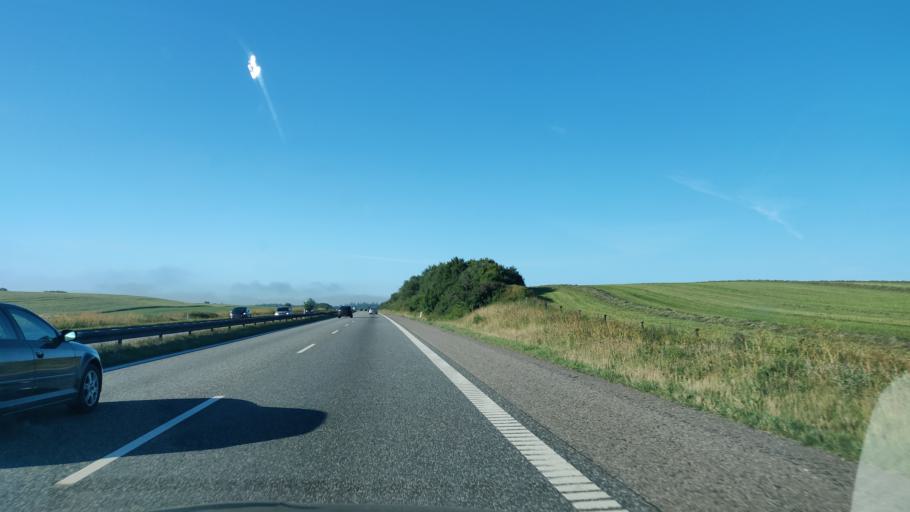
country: DK
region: North Denmark
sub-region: Mariagerfjord Kommune
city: Hobro
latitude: 56.7630
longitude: 9.6936
